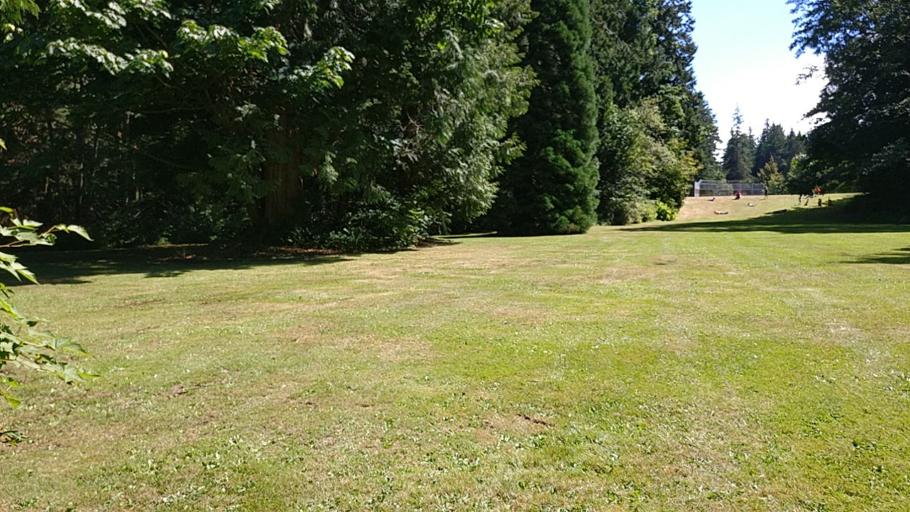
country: CA
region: British Columbia
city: Surrey
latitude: 49.0503
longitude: -122.8605
